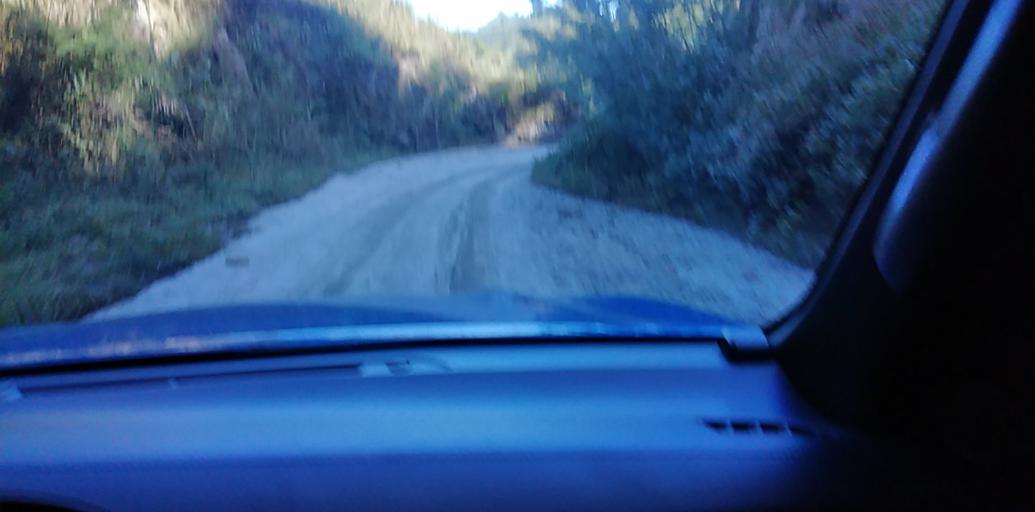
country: PH
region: Central Luzon
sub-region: Province of Pampanga
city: Dolores
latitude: 15.1672
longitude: 120.4721
